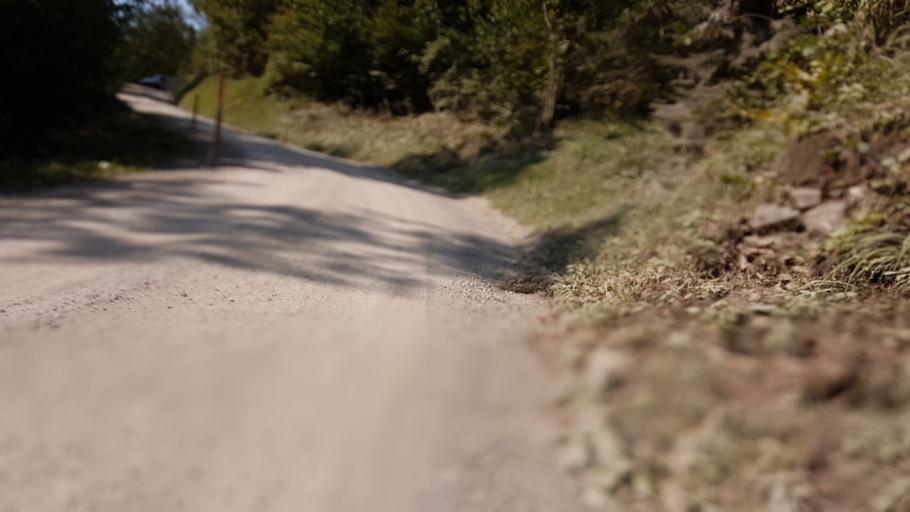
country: CH
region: Bern
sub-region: Frutigen-Niedersimmental District
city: Aeschi
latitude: 46.6325
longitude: 7.7417
